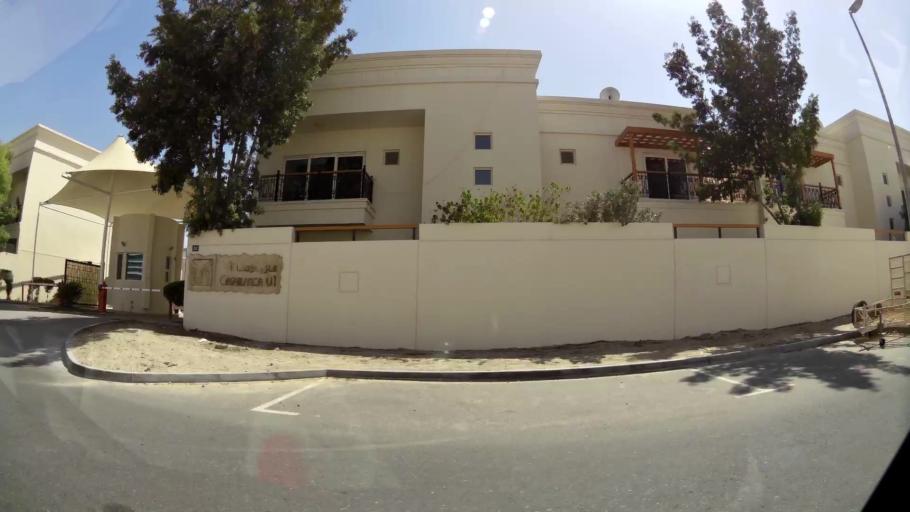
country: AE
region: Dubai
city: Dubai
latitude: 25.1102
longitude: 55.2000
